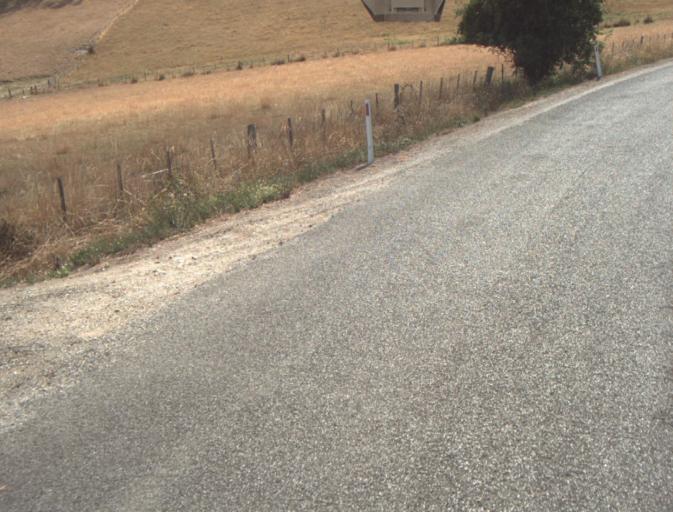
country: AU
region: Tasmania
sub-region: Launceston
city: Mayfield
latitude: -41.2600
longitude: 147.1618
